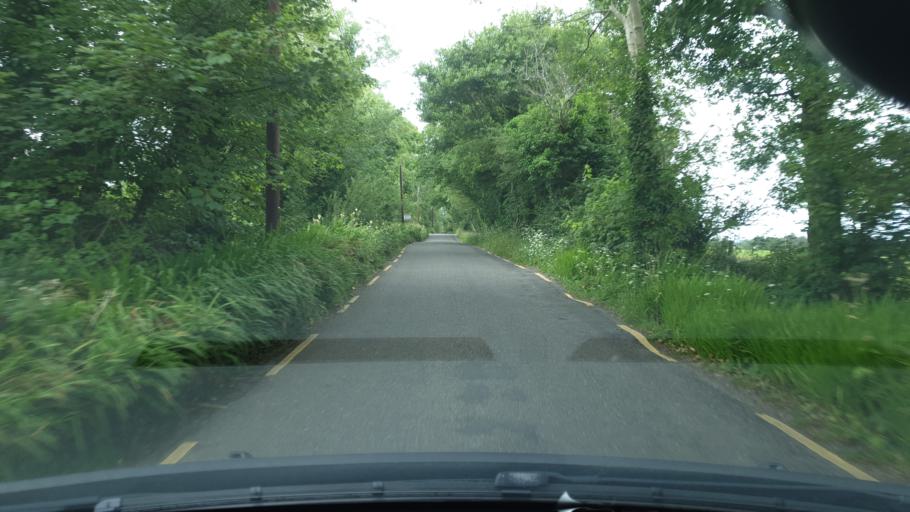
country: IE
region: Munster
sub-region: Ciarrai
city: Tralee
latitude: 52.2422
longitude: -9.6496
